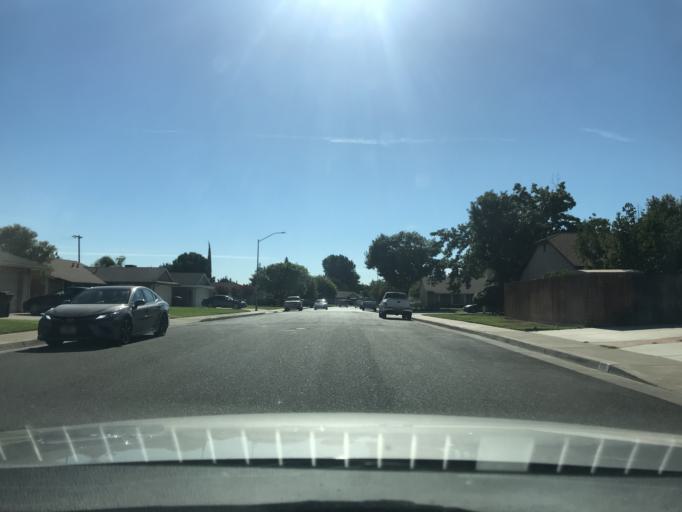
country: US
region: California
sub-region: Merced County
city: Atwater
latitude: 37.3445
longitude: -120.5862
